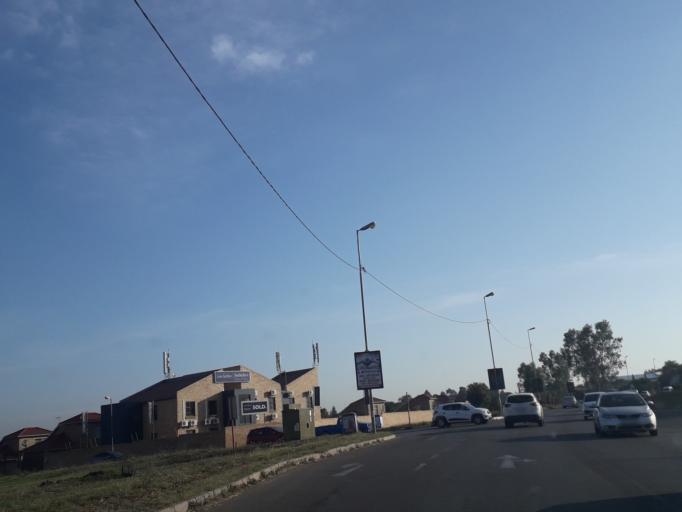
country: ZA
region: Gauteng
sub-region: City of Johannesburg Metropolitan Municipality
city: Roodepoort
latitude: -26.1028
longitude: 27.9002
